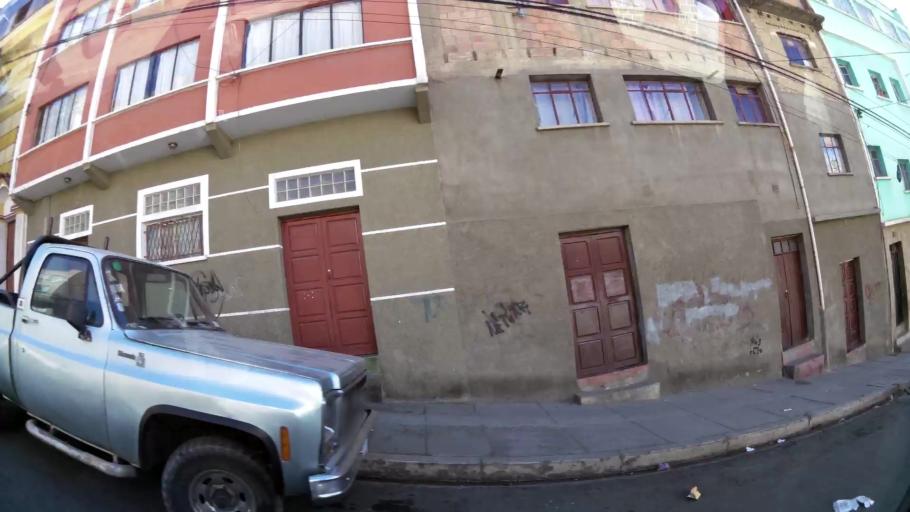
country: BO
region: La Paz
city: La Paz
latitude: -16.5026
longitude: -68.1467
